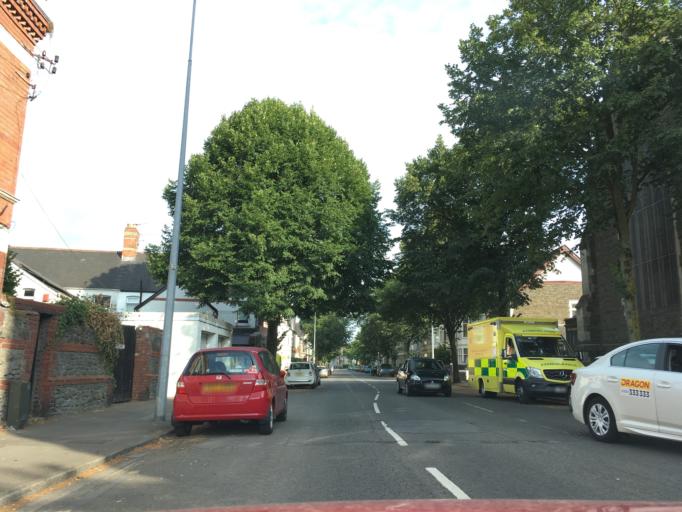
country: GB
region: Wales
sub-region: Cardiff
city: Cardiff
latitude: 51.4962
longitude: -3.1645
